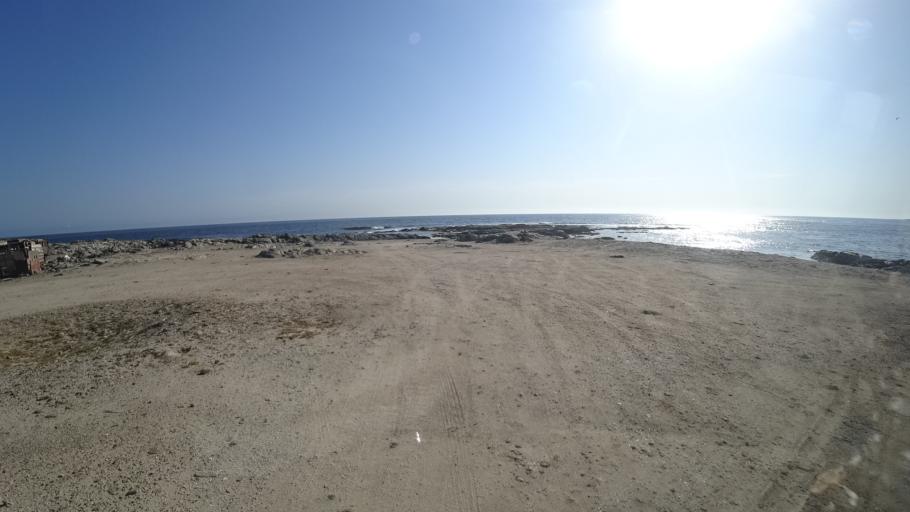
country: OM
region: Zufar
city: Salalah
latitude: 16.9452
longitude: 54.7919
